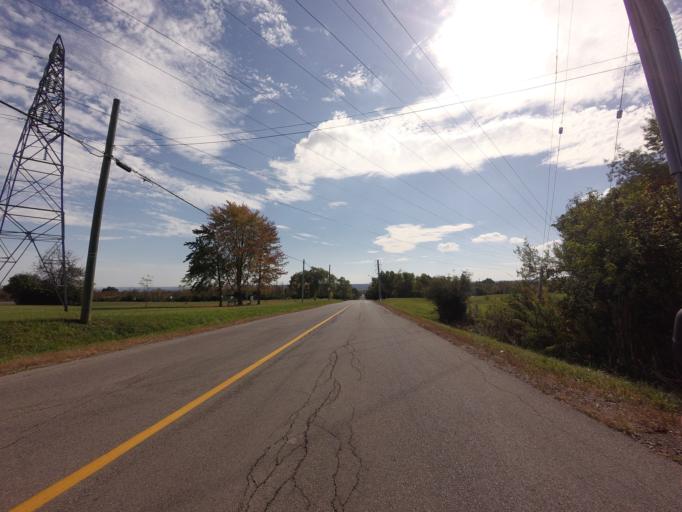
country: CA
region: Ontario
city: Hamilton
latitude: 43.3027
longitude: -79.9093
